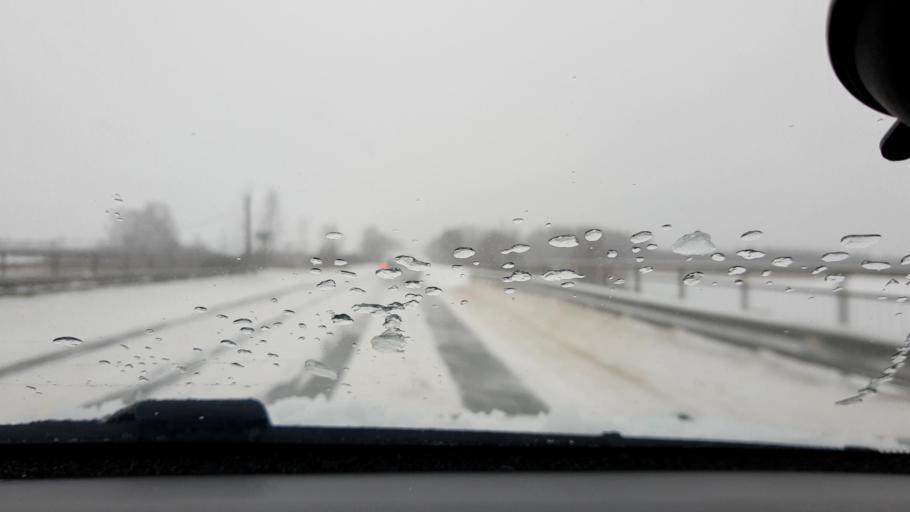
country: RU
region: Nizjnij Novgorod
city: Purekh
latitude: 56.6390
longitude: 43.1084
